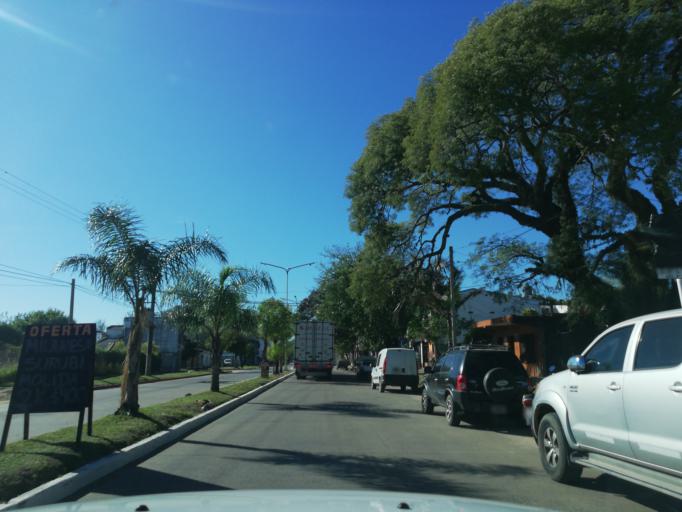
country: AR
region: Corrientes
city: Corrientes
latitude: -27.4762
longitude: -58.7919
